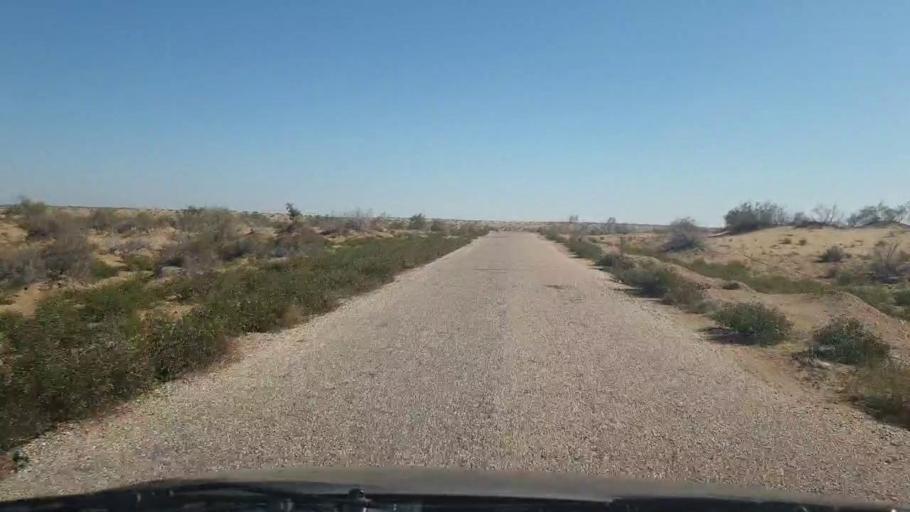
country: PK
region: Sindh
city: Bozdar
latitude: 27.0129
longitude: 68.7903
